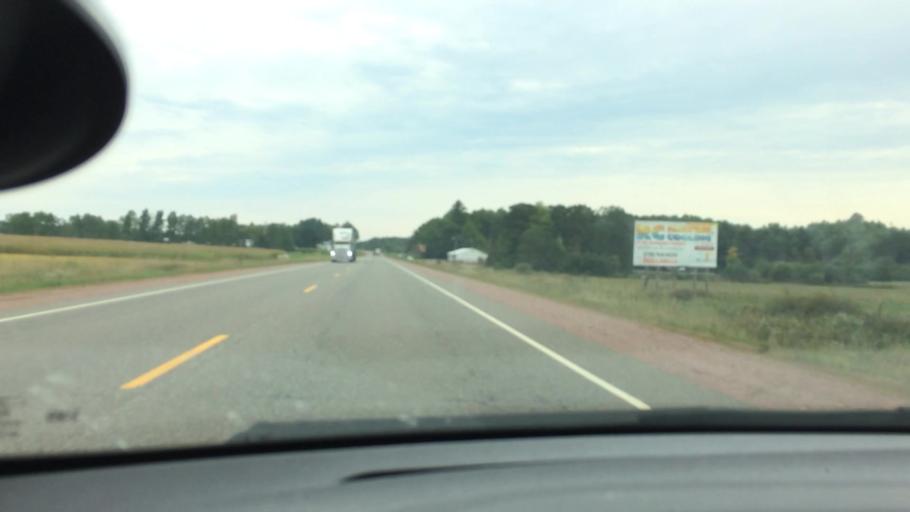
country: US
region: Wisconsin
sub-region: Clark County
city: Neillsville
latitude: 44.5637
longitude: -90.6910
